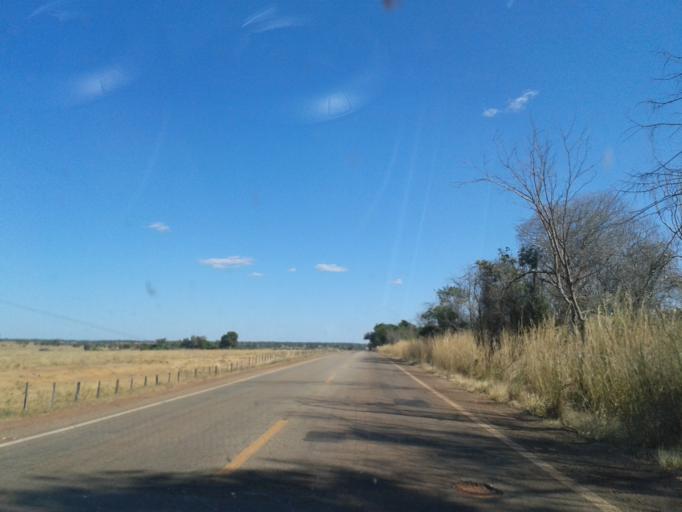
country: BR
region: Goias
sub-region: Mozarlandia
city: Mozarlandia
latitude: -14.3918
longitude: -50.4391
